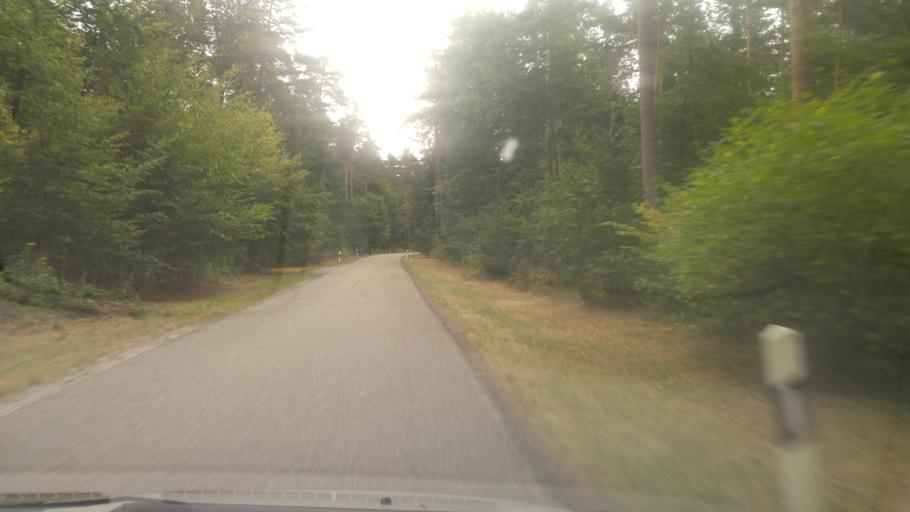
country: DE
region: Rheinland-Pfalz
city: Steinfeld
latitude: 49.0136
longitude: 8.0540
